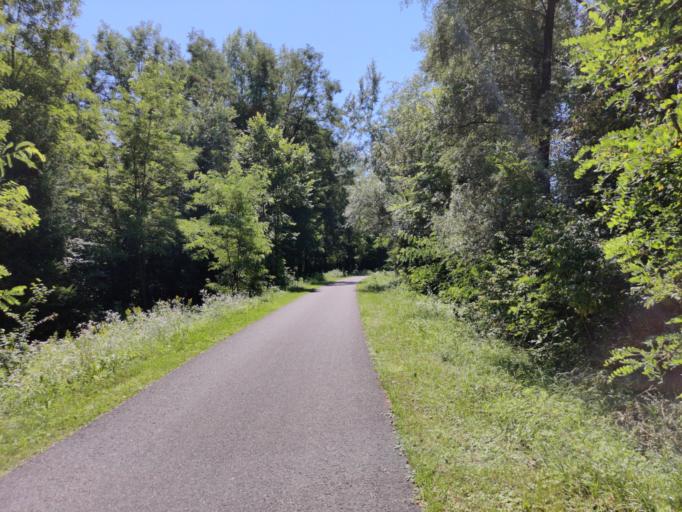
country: AT
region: Styria
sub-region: Politischer Bezirk Leibnitz
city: Obervogau
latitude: 46.7363
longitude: 15.5780
